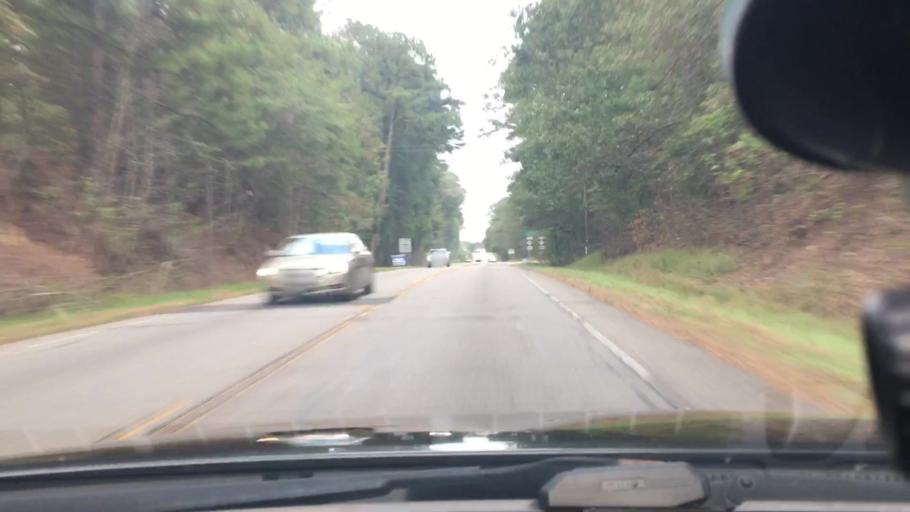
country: US
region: North Carolina
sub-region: Moore County
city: Carthage
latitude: 35.3485
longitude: -79.3677
